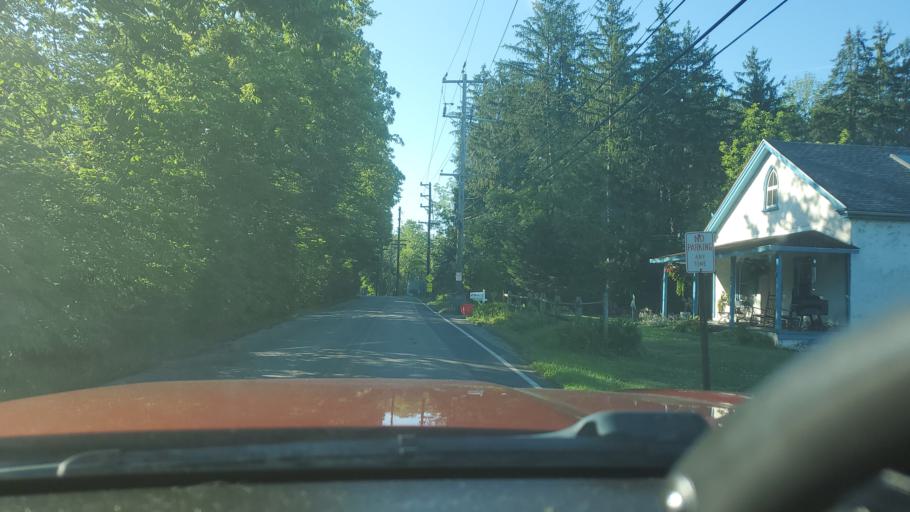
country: US
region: Pennsylvania
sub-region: Montgomery County
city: Woxall
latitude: 40.3239
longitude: -75.4781
